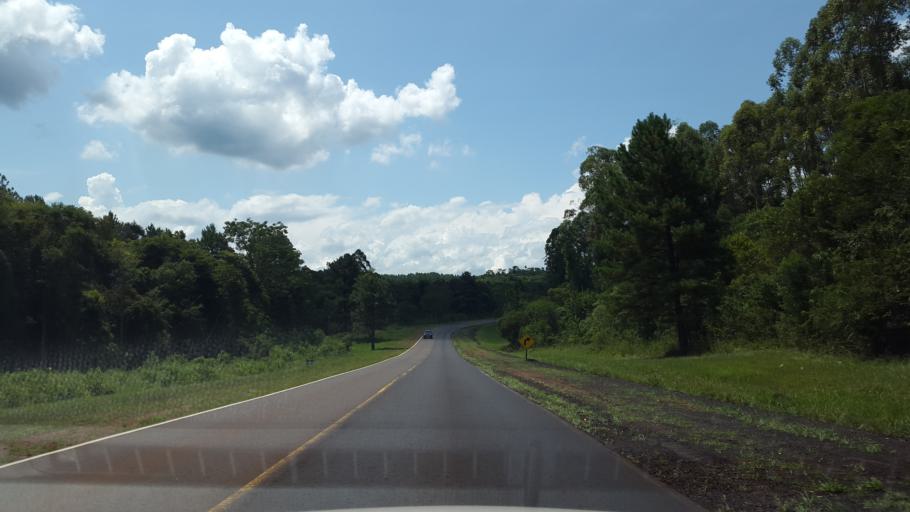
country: AR
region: Misiones
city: El Alcazar
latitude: -26.7352
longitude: -54.8756
